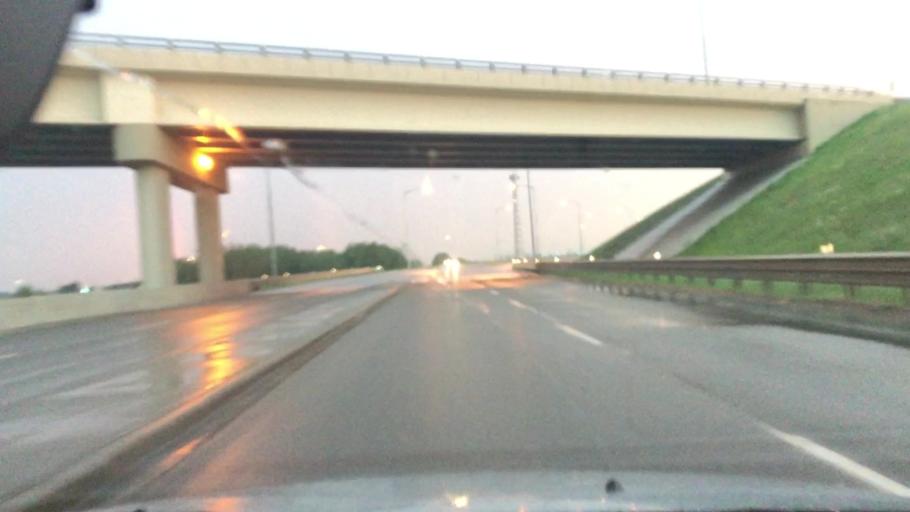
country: CA
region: Alberta
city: St. Albert
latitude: 53.6328
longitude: -113.5658
